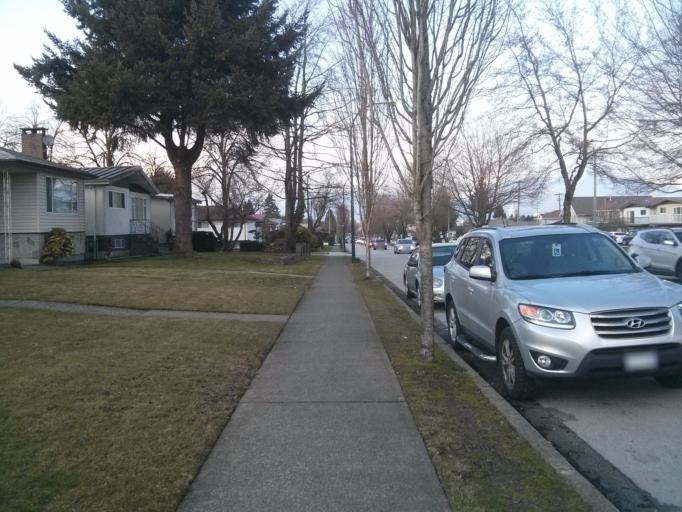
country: CA
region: British Columbia
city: Burnaby
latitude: 49.2455
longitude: -123.0239
